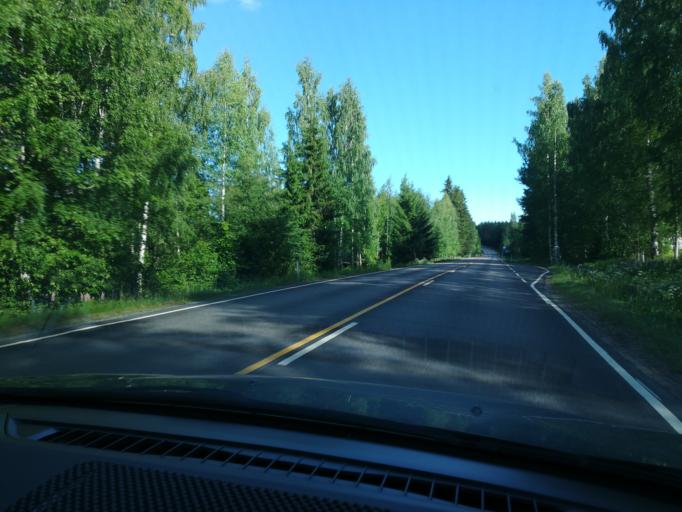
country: FI
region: Southern Savonia
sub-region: Mikkeli
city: Puumala
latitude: 61.5107
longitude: 28.1816
